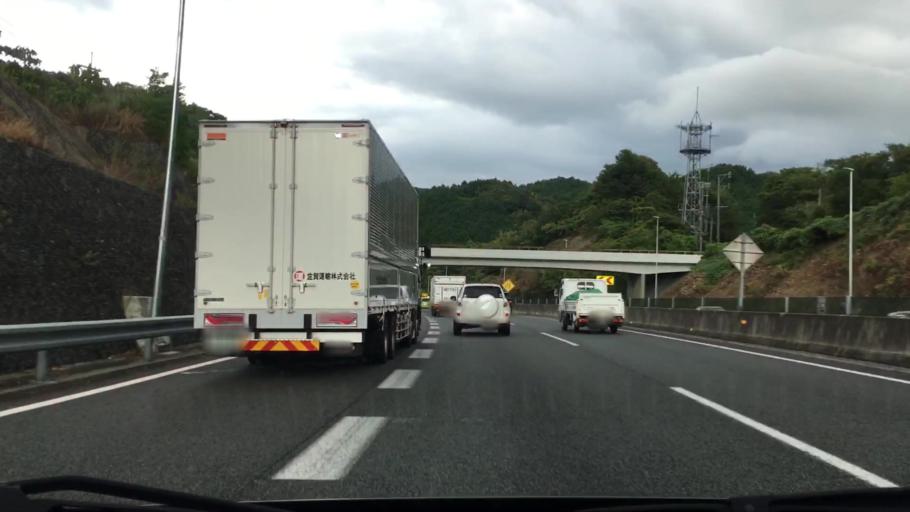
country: JP
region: Fukuoka
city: Nishifukuma
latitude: 33.7491
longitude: 130.5560
